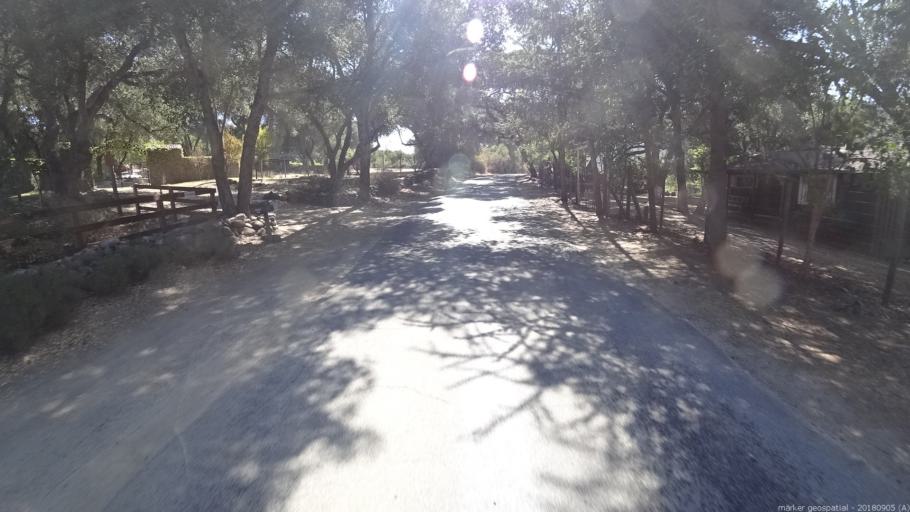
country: US
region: California
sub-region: Monterey County
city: Carmel Valley Village
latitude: 36.4033
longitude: -121.6604
